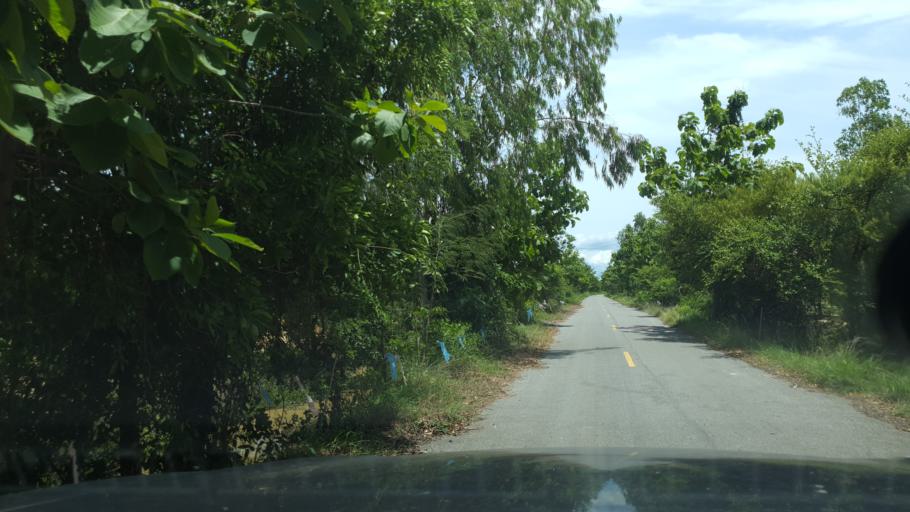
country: TH
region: Sukhothai
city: Ban Na
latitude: 17.1121
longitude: 99.6776
